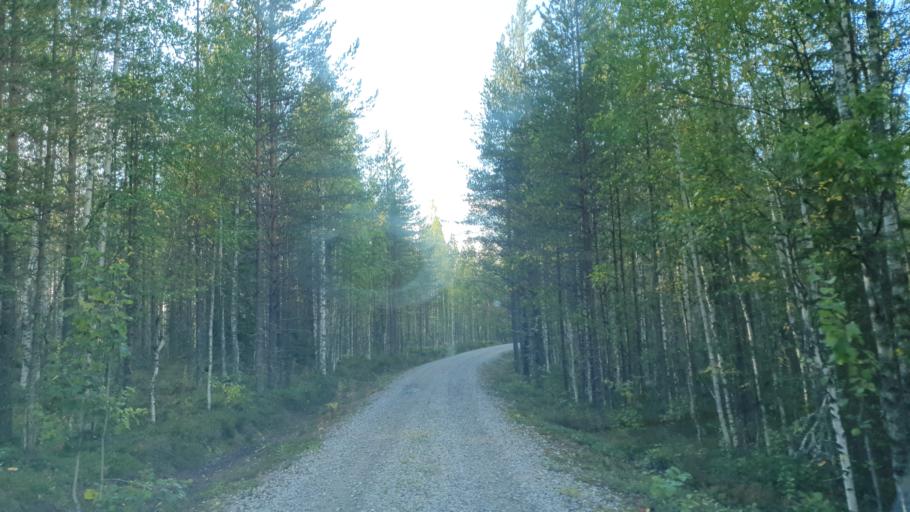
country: FI
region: Kainuu
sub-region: Kehys-Kainuu
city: Kuhmo
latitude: 64.3275
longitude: 30.0362
